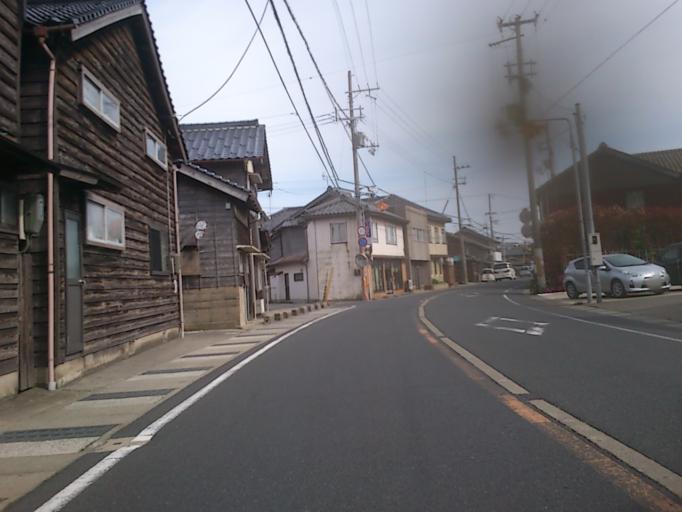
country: JP
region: Kyoto
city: Miyazu
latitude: 35.6854
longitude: 135.0241
